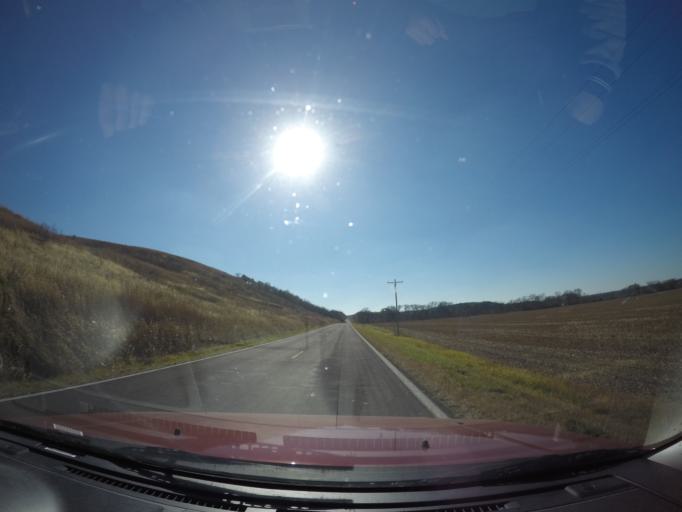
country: US
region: Kansas
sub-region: Geary County
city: Grandview Plaza
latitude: 39.0037
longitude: -96.7305
